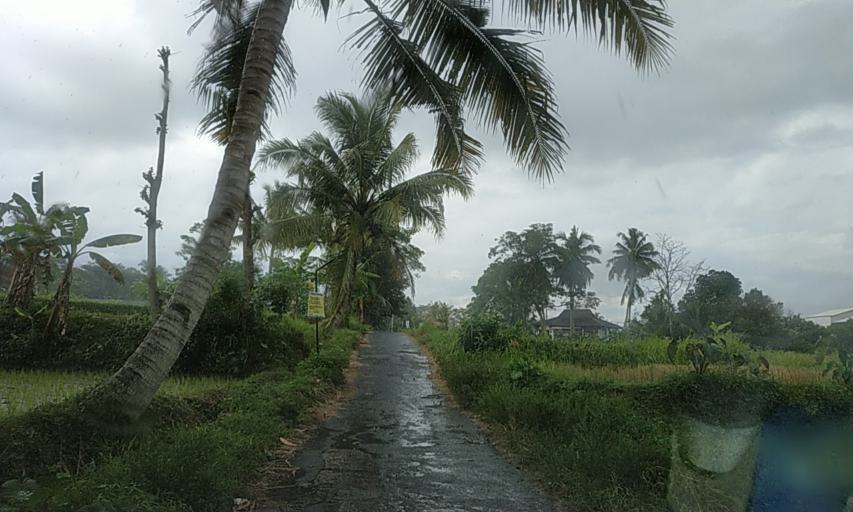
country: ID
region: Daerah Istimewa Yogyakarta
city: Sleman
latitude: -7.6748
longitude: 110.4159
